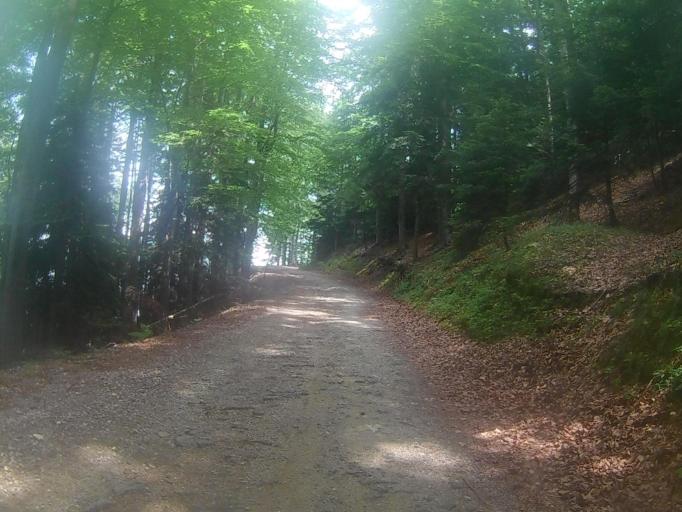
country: SI
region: Ruse
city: Bistrica ob Dravi
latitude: 46.5169
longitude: 15.5539
